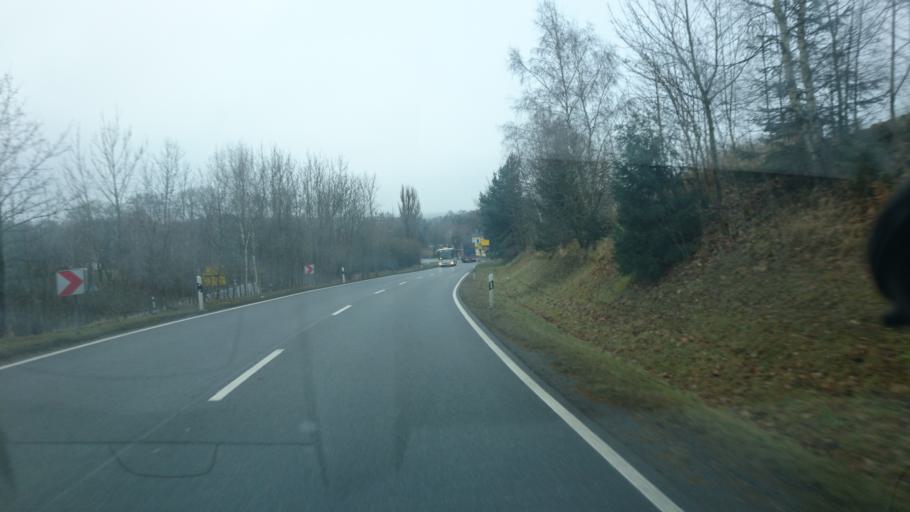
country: DE
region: Bavaria
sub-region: Upper Franconia
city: Topen
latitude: 50.4239
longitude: 11.8514
